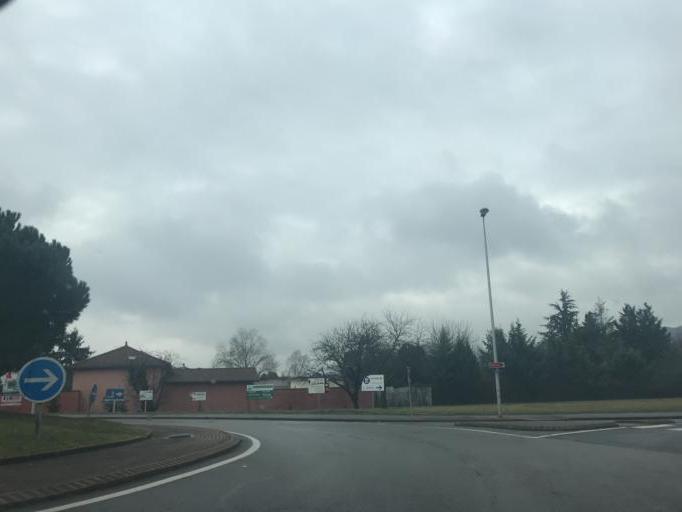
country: FR
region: Rhone-Alpes
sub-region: Departement du Rhone
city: Genay
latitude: 45.8955
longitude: 4.8206
